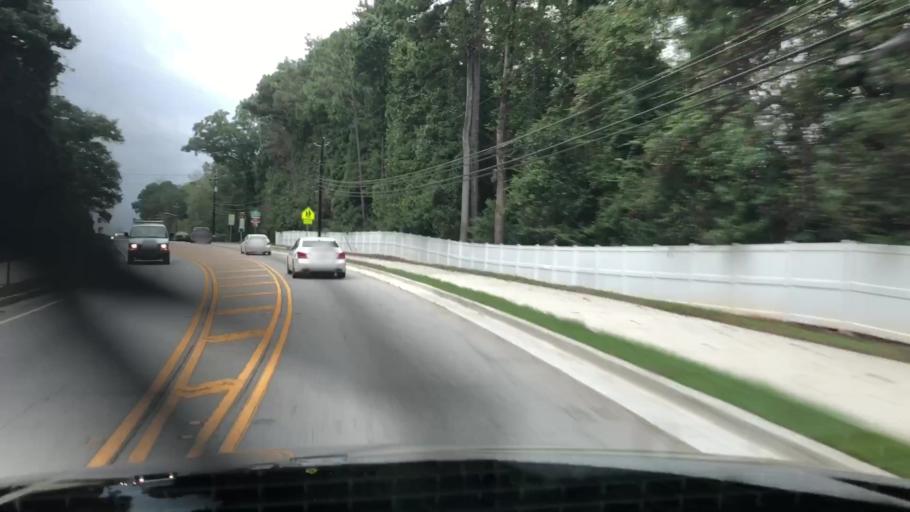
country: US
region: Georgia
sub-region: Cobb County
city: Mableton
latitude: 33.7079
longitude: -84.5603
